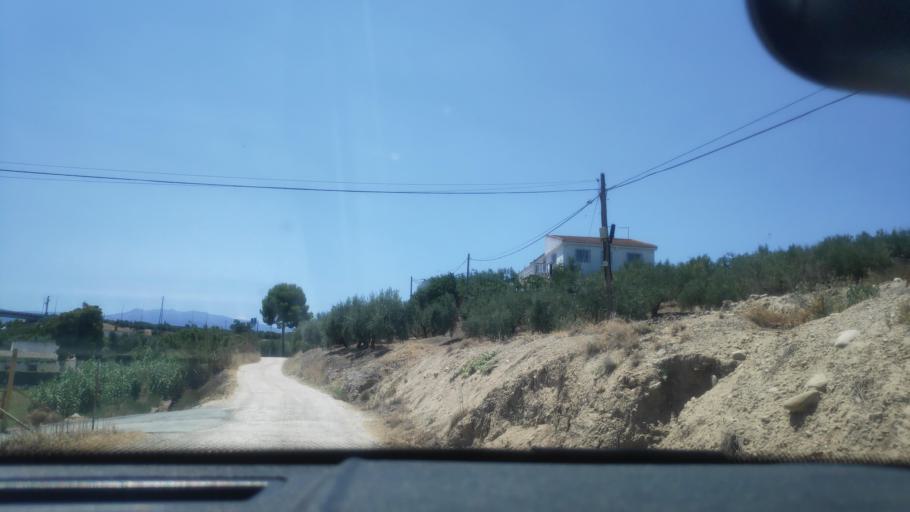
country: ES
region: Andalusia
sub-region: Provincia de Jaen
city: Jaen
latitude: 37.8238
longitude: -3.7592
